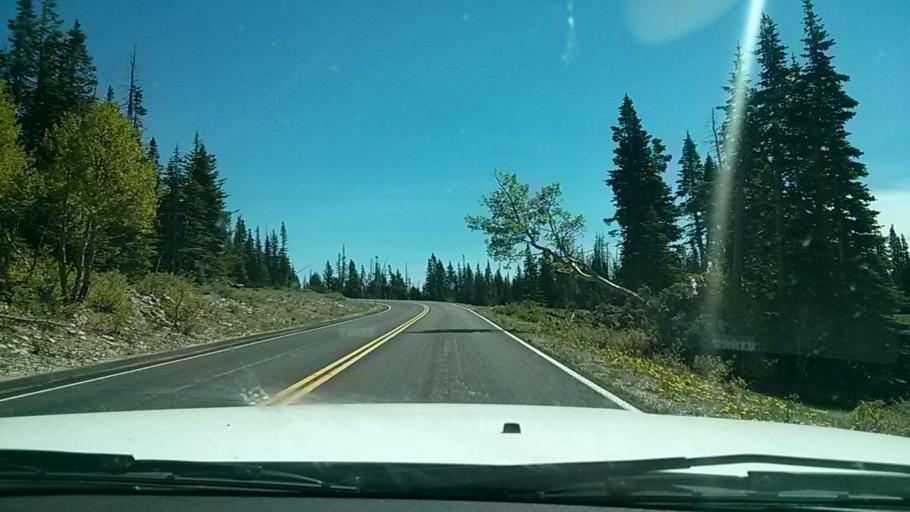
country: US
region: Utah
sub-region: Iron County
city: Parowan
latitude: 37.6340
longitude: -112.8244
